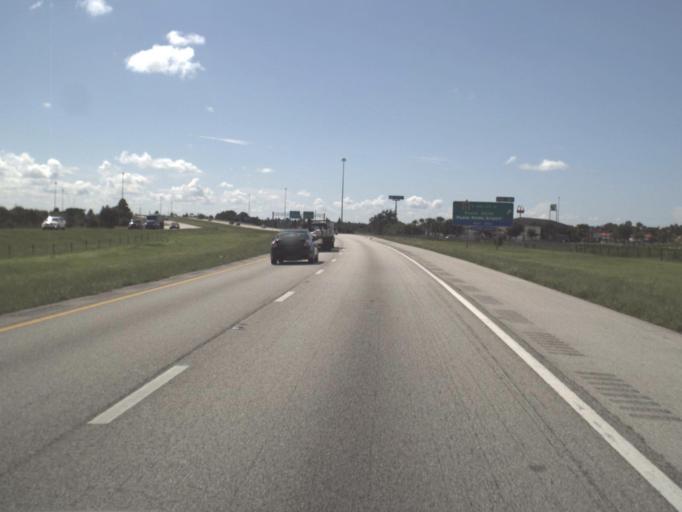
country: US
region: Florida
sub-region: Charlotte County
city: Charlotte Park
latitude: 26.9012
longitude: -82.0077
